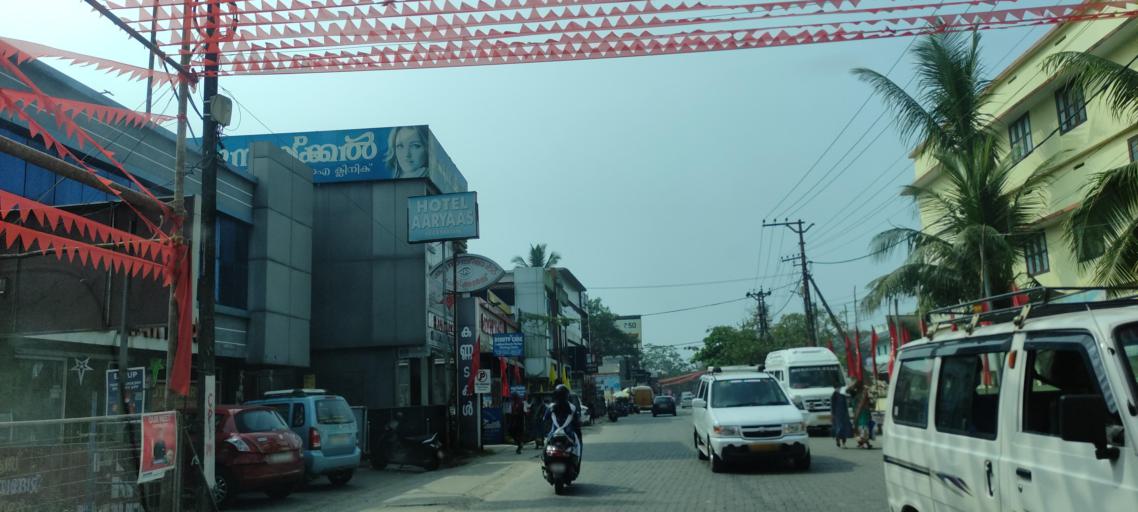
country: IN
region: Kerala
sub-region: Alappuzha
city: Shertallai
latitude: 9.6859
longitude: 76.3446
